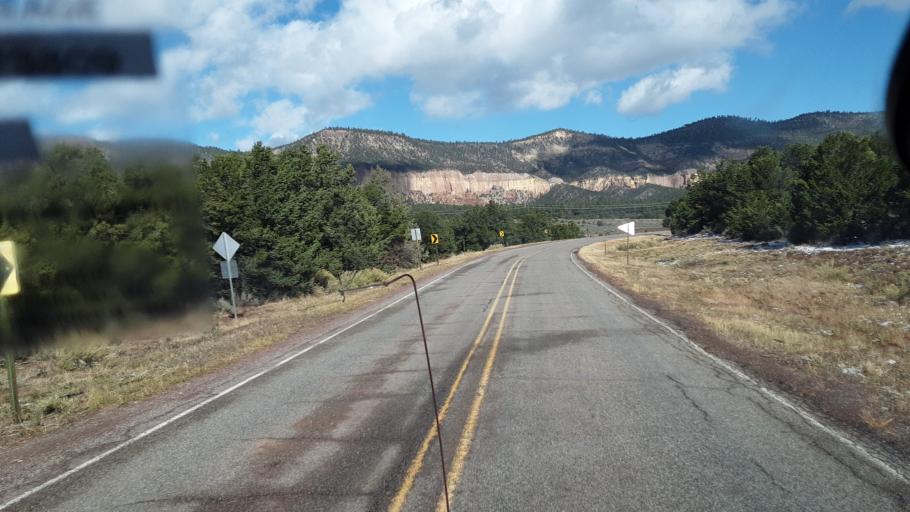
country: US
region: New Mexico
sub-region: Rio Arriba County
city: Santa Teresa
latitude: 36.1972
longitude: -106.7391
